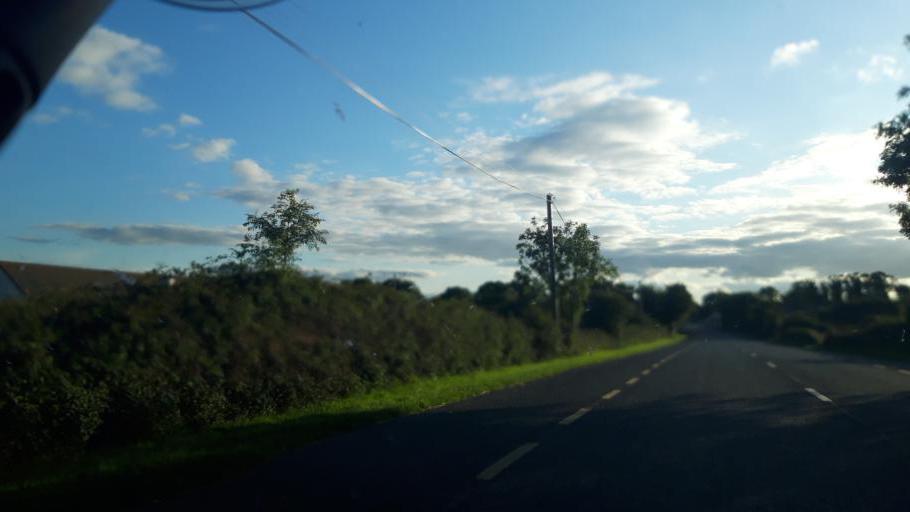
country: IE
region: Leinster
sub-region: Lu
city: Carlingford
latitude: 54.0146
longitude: -6.1587
